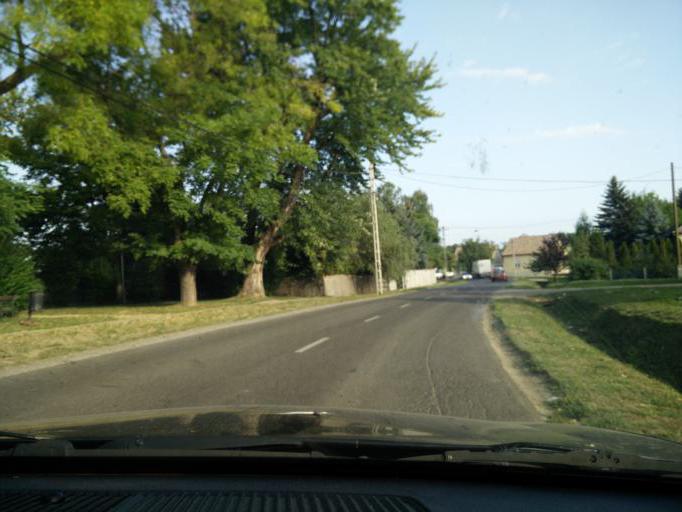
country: HU
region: Baranya
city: Szaszvar
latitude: 46.2723
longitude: 18.3835
